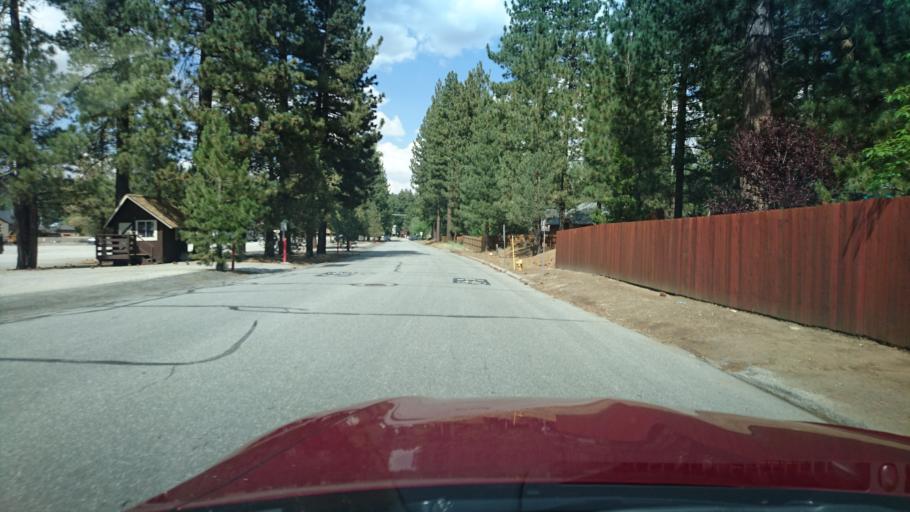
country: US
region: California
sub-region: San Bernardino County
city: Big Bear Lake
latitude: 34.2428
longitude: -116.8848
